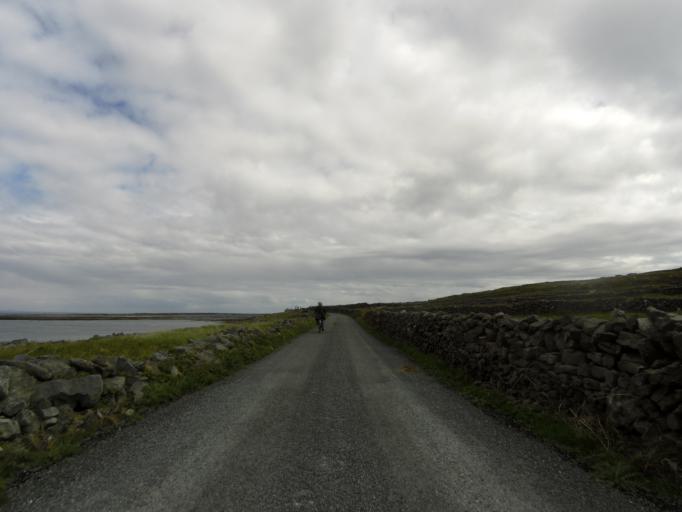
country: IE
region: Connaught
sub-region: County Galway
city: Clifden
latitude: 53.1374
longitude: -9.7167
